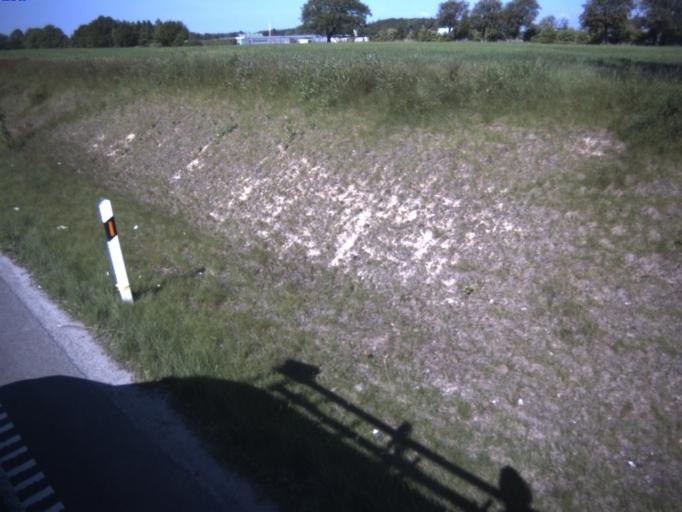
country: SE
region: Skane
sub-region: Helsingborg
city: Odakra
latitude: 56.0421
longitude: 12.7573
